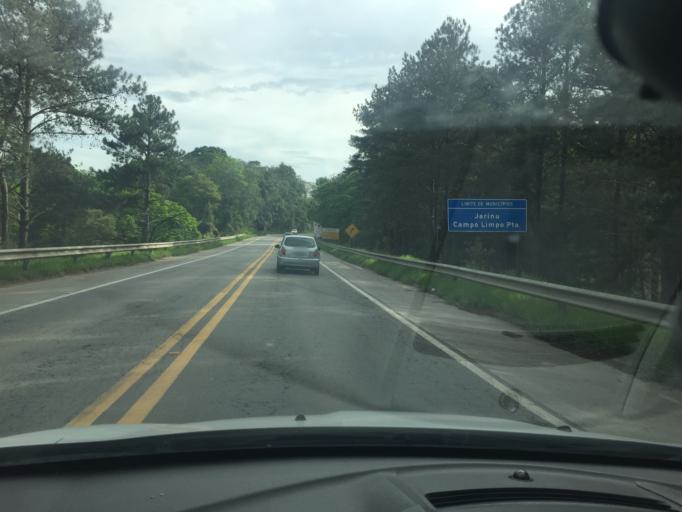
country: BR
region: Sao Paulo
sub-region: Campo Limpo Paulista
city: Campo Limpo Paulista
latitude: -23.1748
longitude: -46.7740
